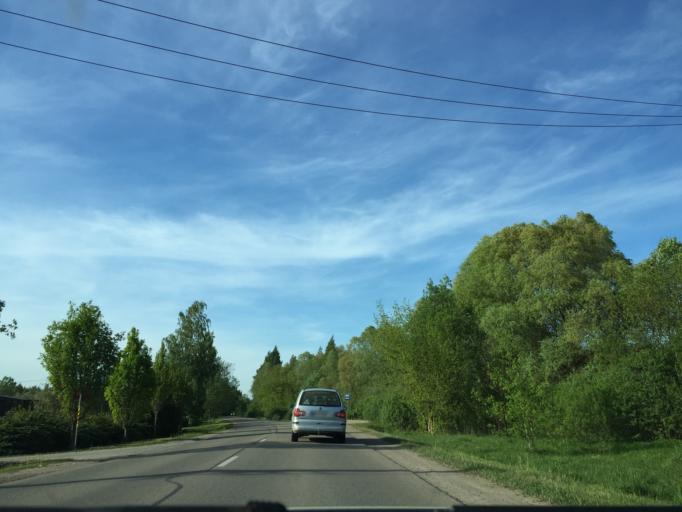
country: LV
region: Jelgava
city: Jelgava
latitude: 56.6048
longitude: 23.6810
